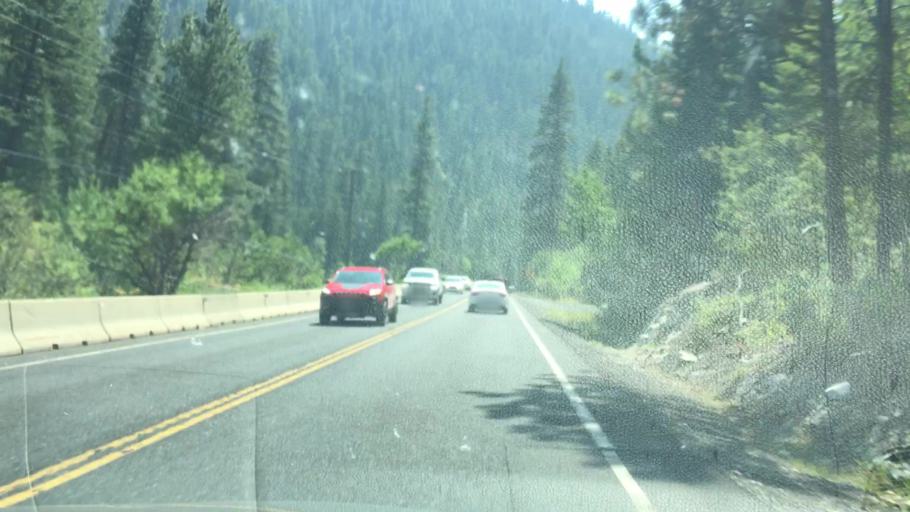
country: US
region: Idaho
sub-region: Valley County
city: McCall
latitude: 45.1331
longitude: -116.2848
